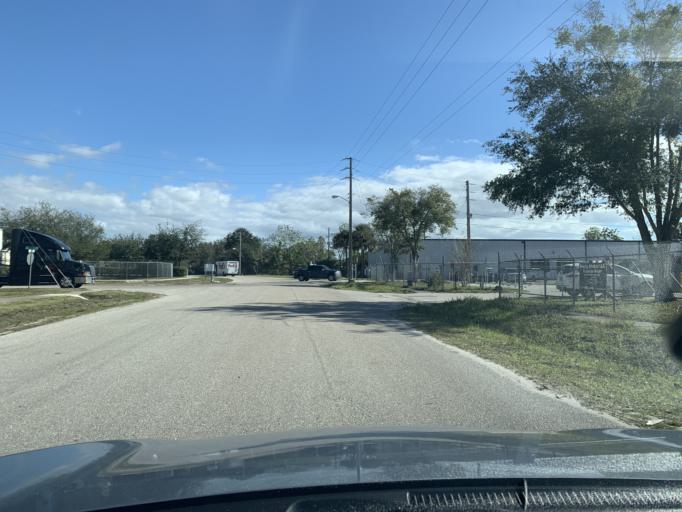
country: US
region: Florida
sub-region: Orange County
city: Lockhart
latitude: 28.6306
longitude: -81.4672
